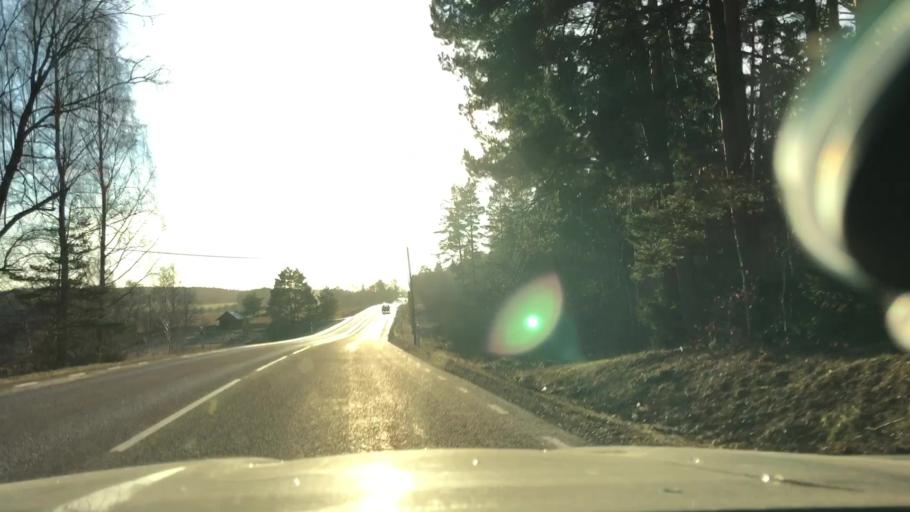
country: SE
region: Stockholm
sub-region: Sodertalje Kommun
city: Pershagen
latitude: 59.0417
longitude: 17.6035
